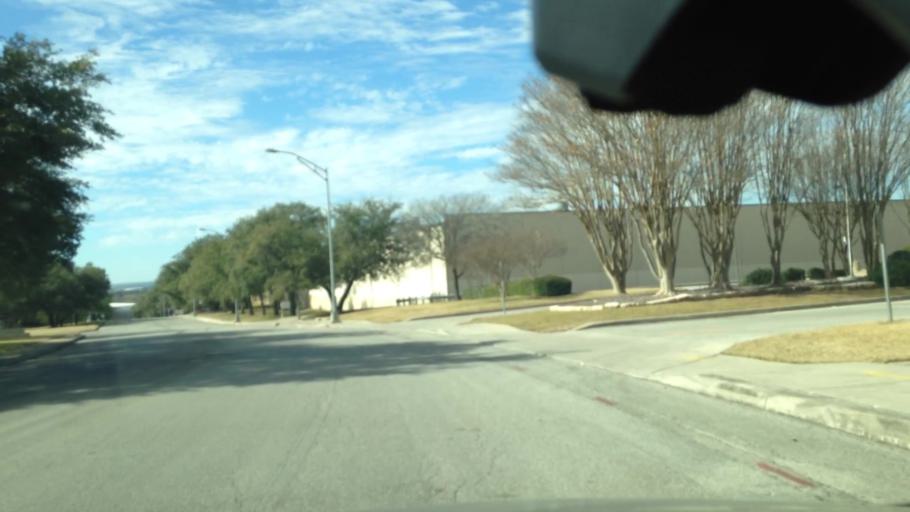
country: US
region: Texas
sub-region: Bexar County
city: Shavano Park
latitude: 29.5539
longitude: -98.5900
